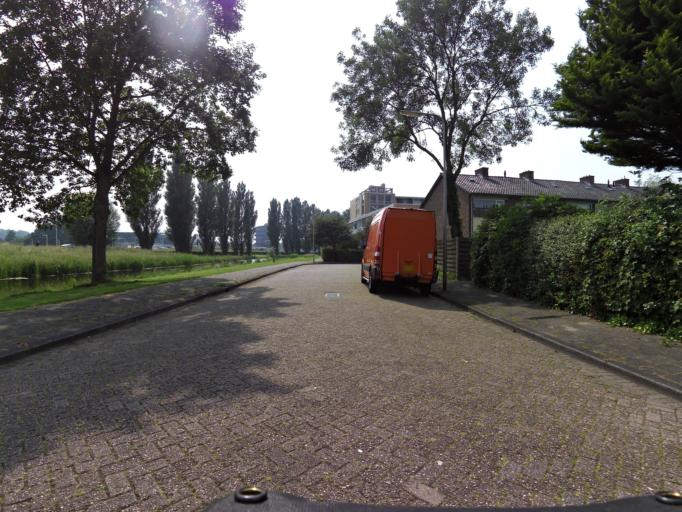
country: NL
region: South Holland
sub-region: Gemeente Spijkenisse
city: Spijkenisse
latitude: 51.8518
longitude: 4.3131
